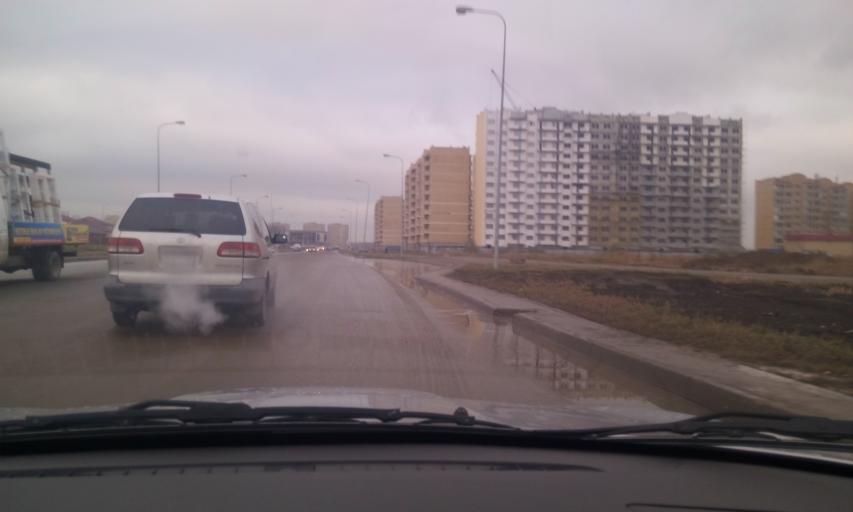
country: KZ
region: Astana Qalasy
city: Astana
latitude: 51.1754
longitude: 71.3666
